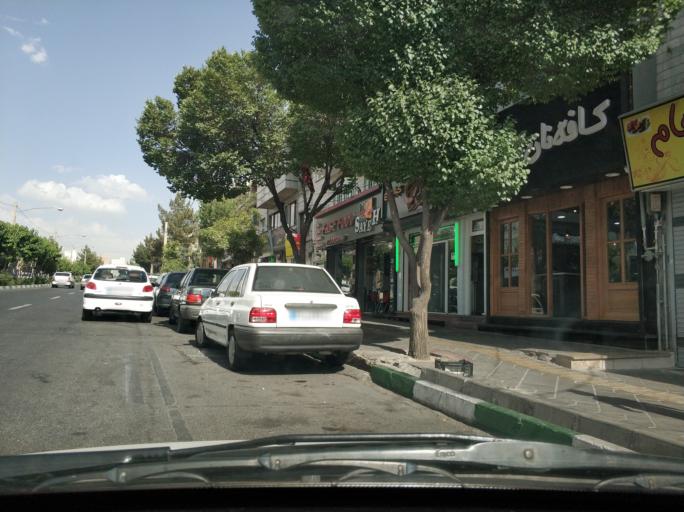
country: IR
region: Tehran
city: Tehran
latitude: 35.7417
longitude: 51.5879
